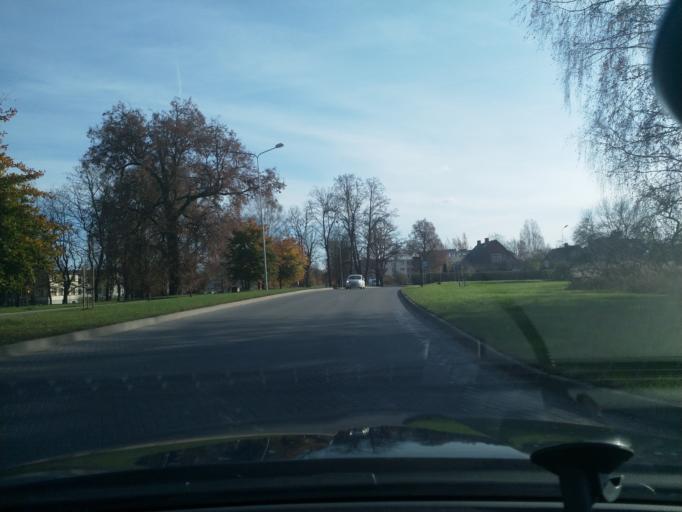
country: LV
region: Kuldigas Rajons
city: Kuldiga
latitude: 56.9637
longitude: 21.9644
